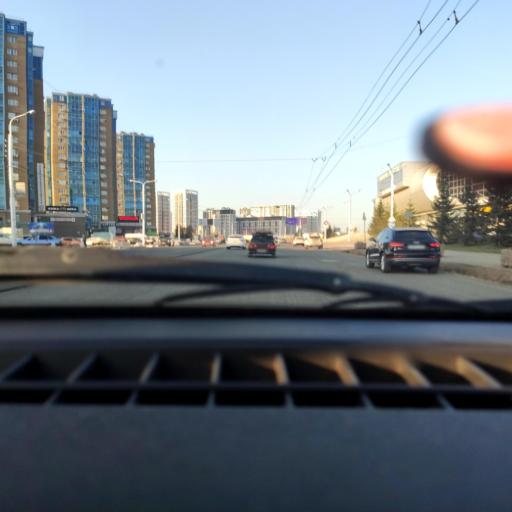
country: RU
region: Bashkortostan
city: Ufa
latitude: 54.7511
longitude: 56.0317
